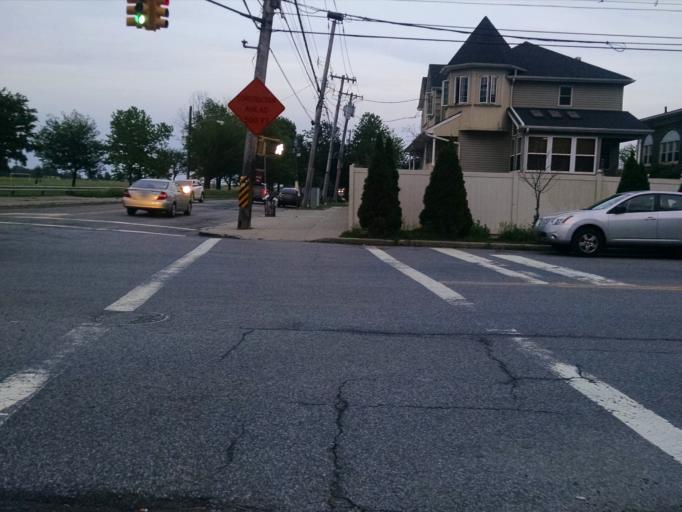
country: US
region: New York
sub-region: Richmond County
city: Staten Island
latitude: 40.5687
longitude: -74.1067
